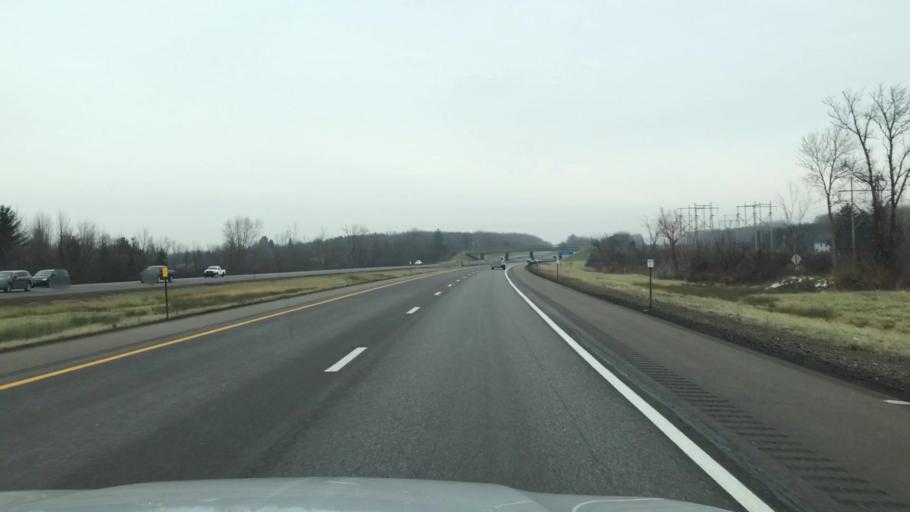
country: US
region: New York
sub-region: Erie County
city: Angola
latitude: 42.6097
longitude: -79.0213
